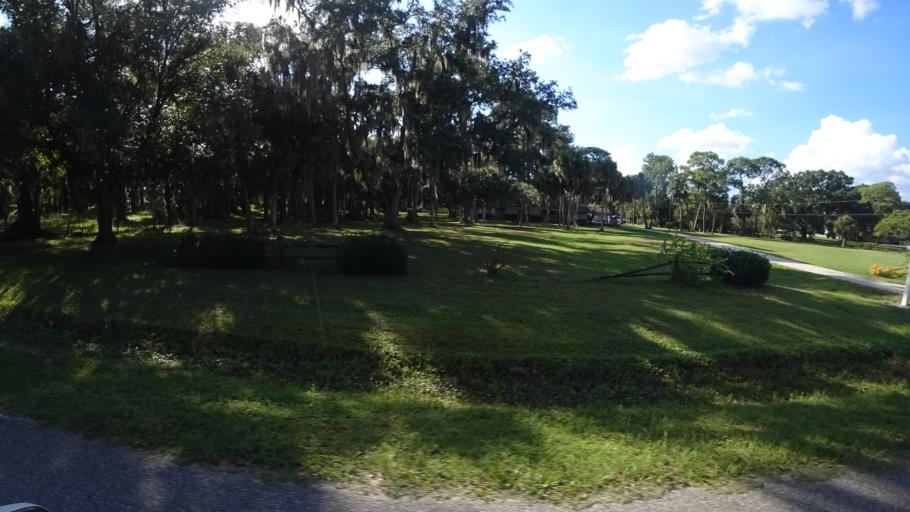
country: US
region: Florida
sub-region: Manatee County
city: Samoset
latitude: 27.4795
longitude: -82.4796
